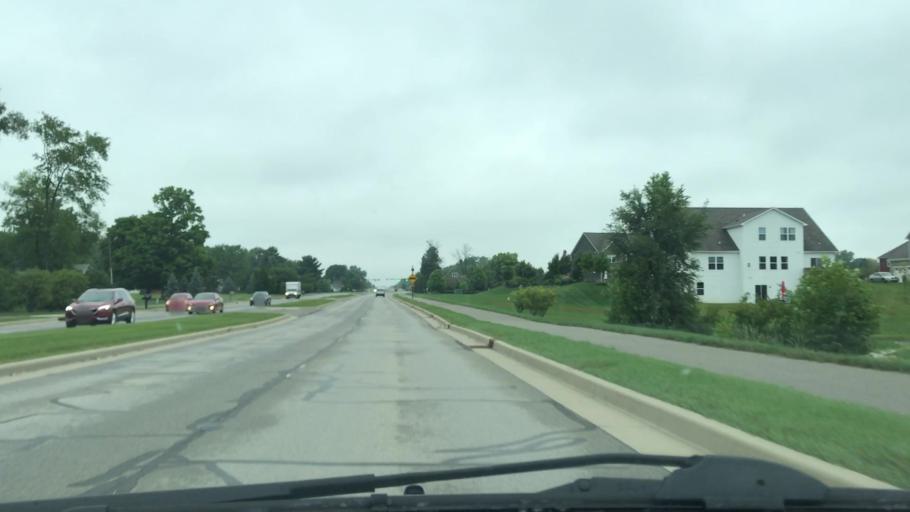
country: US
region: Indiana
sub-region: Hamilton County
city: Westfield
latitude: 40.0291
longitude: -86.0706
